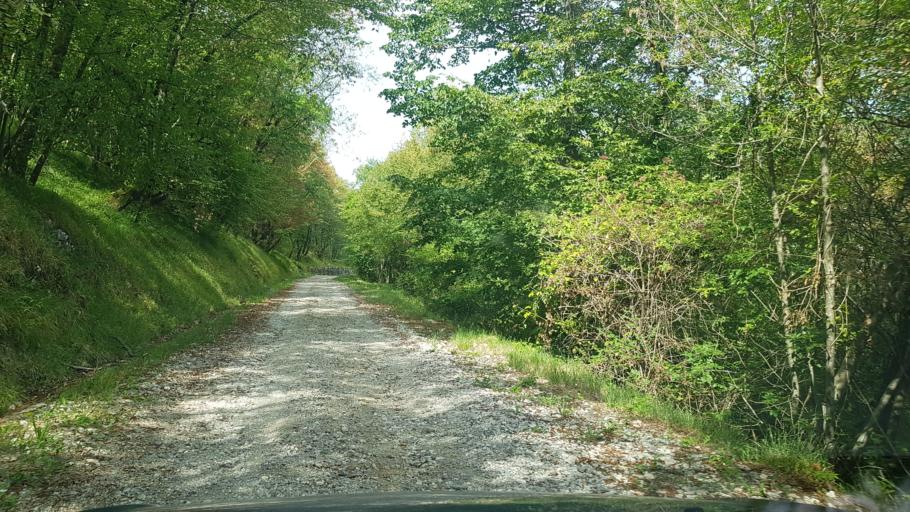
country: SI
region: Nova Gorica
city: Solkan
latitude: 46.0065
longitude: 13.6470
